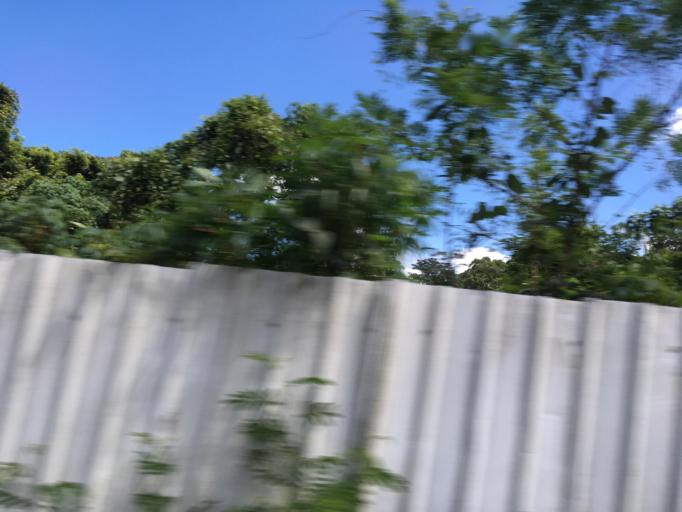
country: TW
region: Taipei
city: Taipei
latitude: 24.9497
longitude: 121.5540
